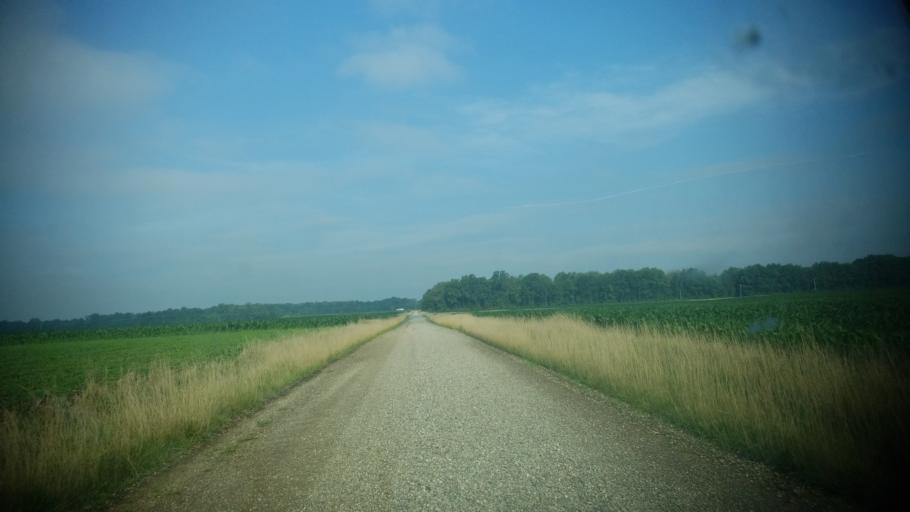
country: US
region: Illinois
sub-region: Clay County
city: Flora
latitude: 38.6018
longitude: -88.3529
